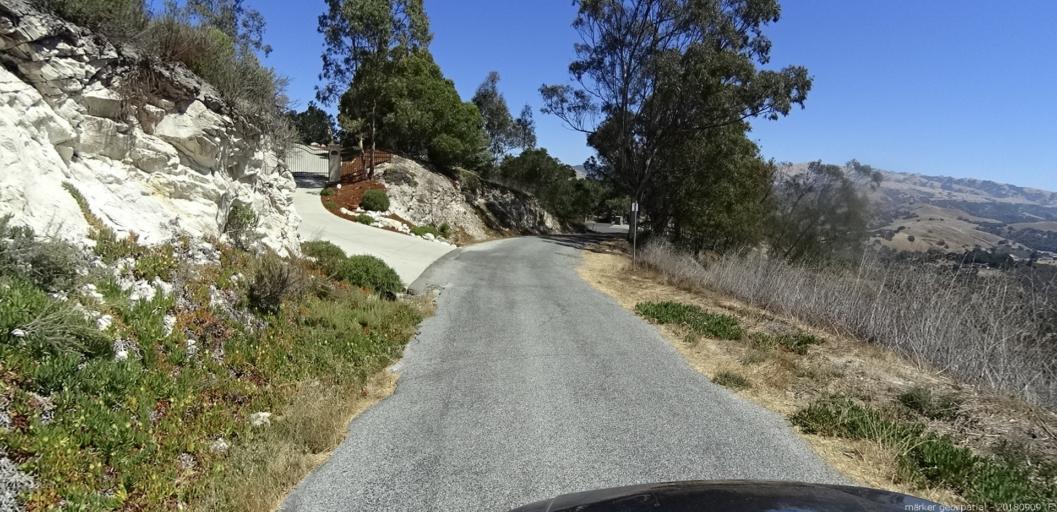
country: US
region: California
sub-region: Monterey County
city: Carmel Valley Village
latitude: 36.5503
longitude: -121.7453
